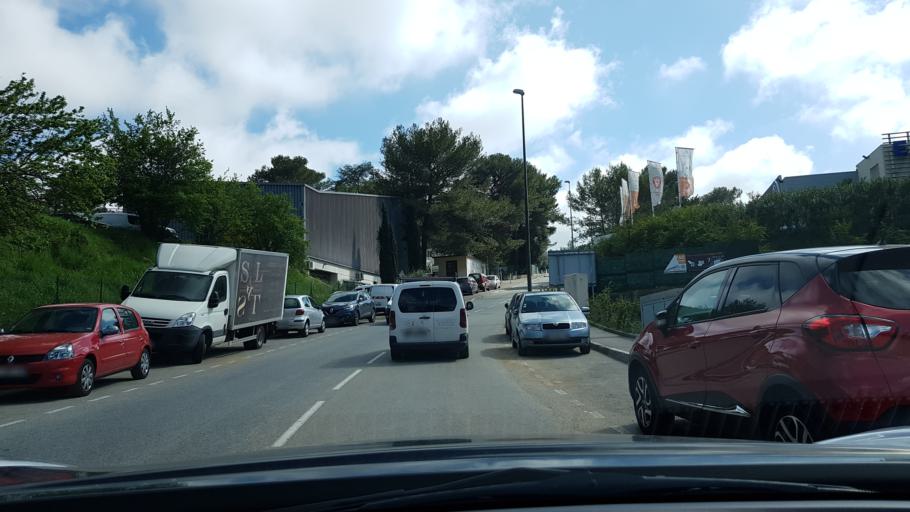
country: FR
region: Provence-Alpes-Cote d'Azur
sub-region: Departement des Alpes-Maritimes
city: Biot
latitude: 43.6045
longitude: 7.0770
